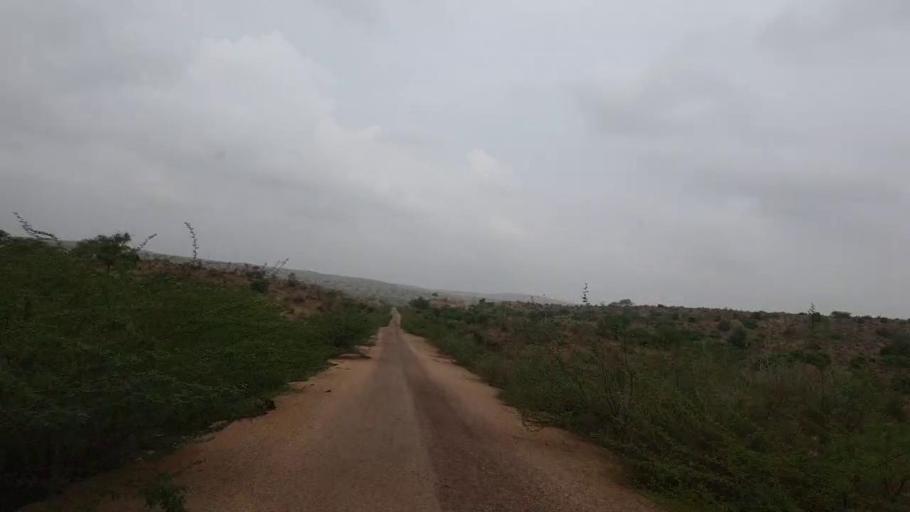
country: PK
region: Sindh
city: Diplo
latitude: 24.5132
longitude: 69.4796
